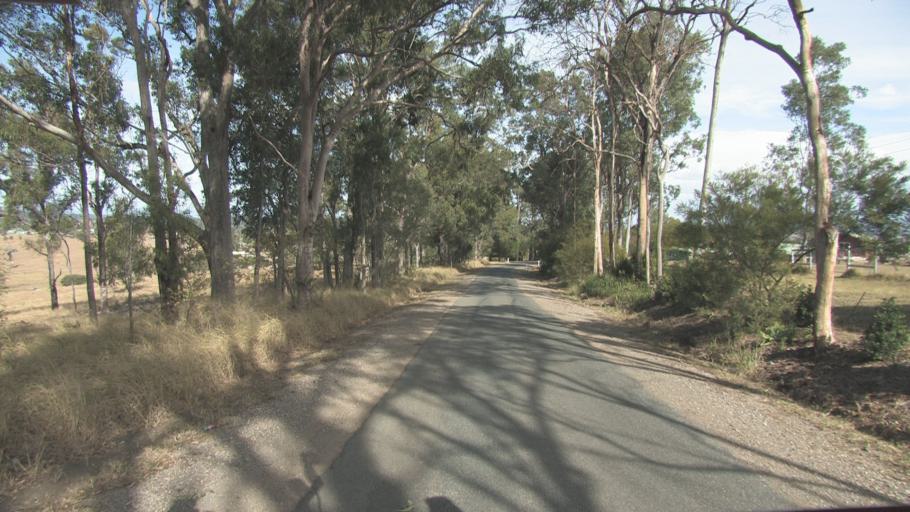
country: AU
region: Queensland
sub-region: Logan
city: Cedar Vale
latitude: -27.9072
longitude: 152.9857
